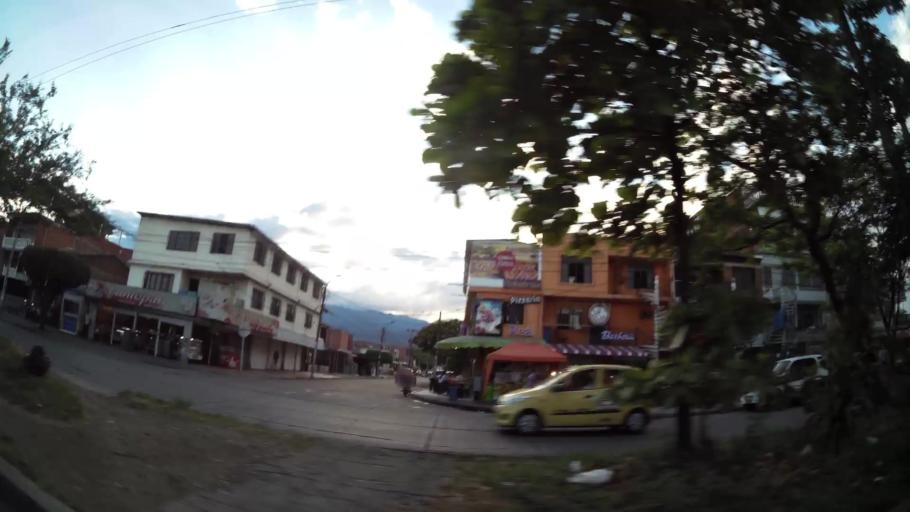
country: CO
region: Valle del Cauca
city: Cali
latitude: 3.4270
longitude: -76.5167
